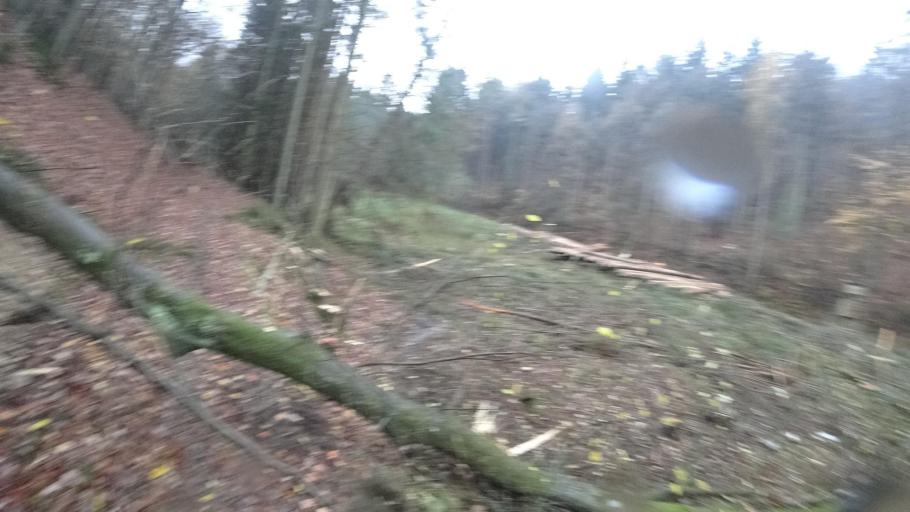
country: DE
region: Rheinland-Pfalz
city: Bad Neuenahr-Ahrweiler
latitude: 50.5140
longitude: 7.0937
